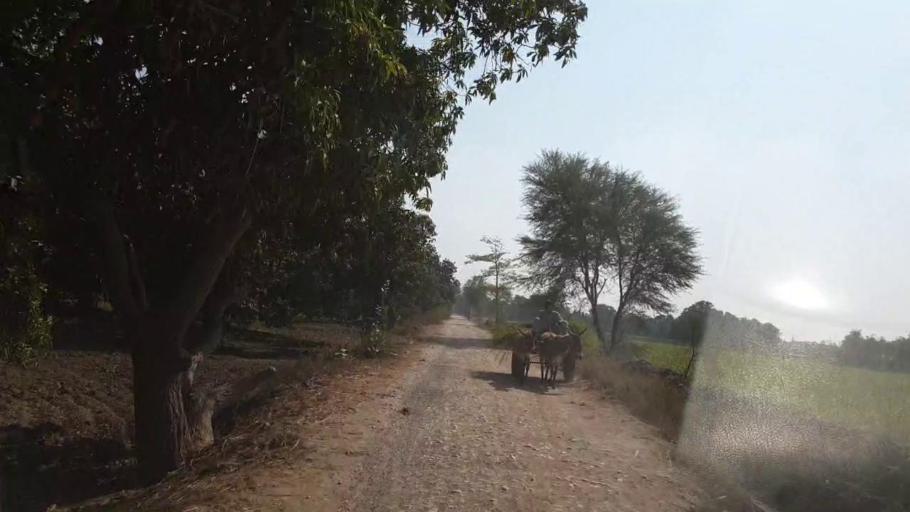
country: PK
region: Sindh
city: Matiari
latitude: 25.5076
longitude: 68.4644
